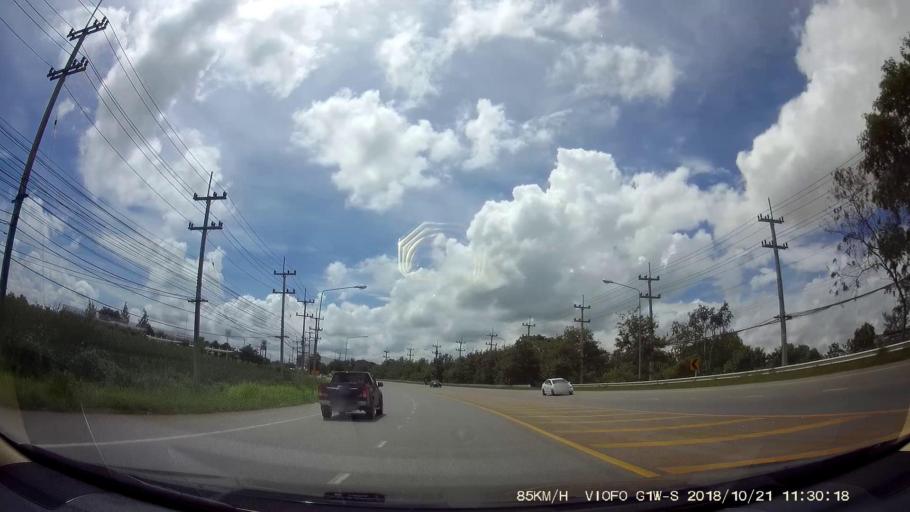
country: TH
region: Chaiyaphum
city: Chaiyaphum
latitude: 15.7802
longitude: 102.0254
